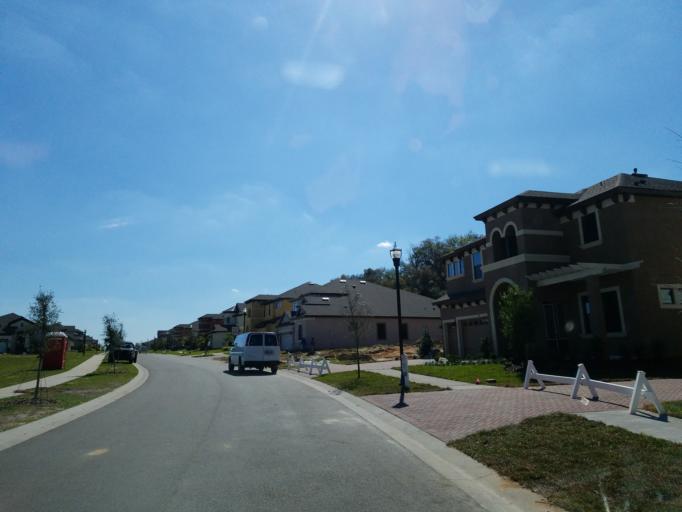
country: US
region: Florida
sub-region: Hillsborough County
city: Brandon
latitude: 27.9299
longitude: -82.2687
